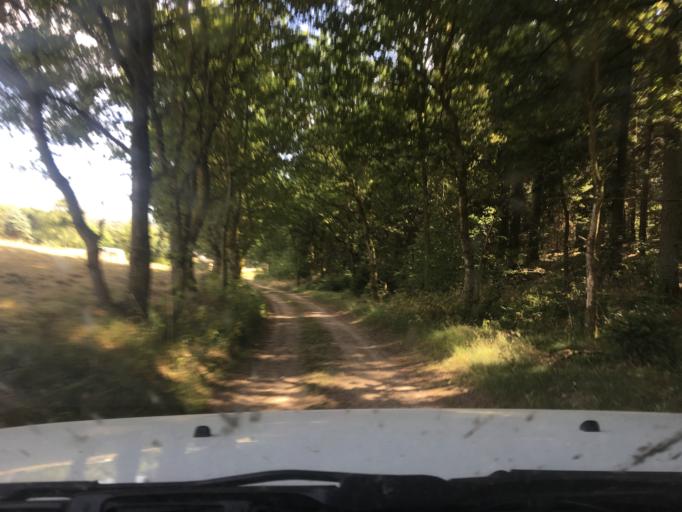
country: DK
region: Central Jutland
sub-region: Viborg Kommune
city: Viborg
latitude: 56.4343
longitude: 9.4583
